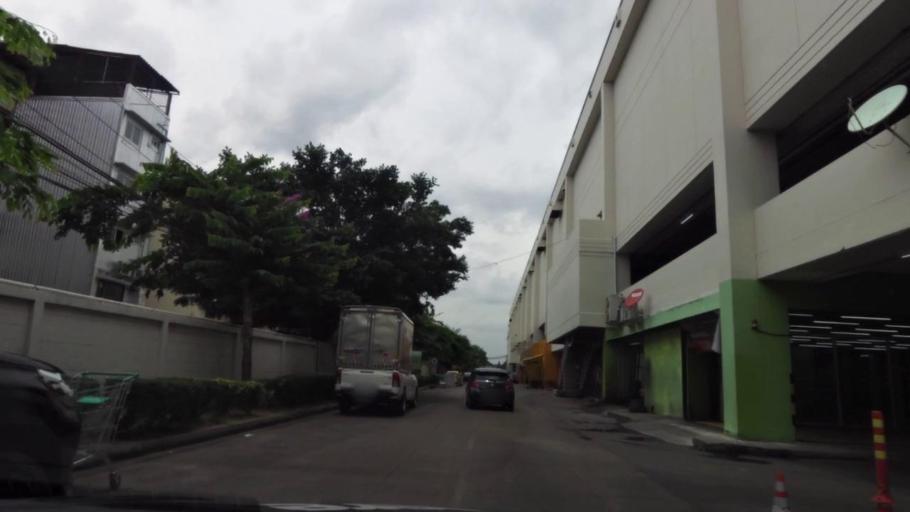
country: TH
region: Bangkok
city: Bang Kapi
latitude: 13.7683
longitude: 100.6435
